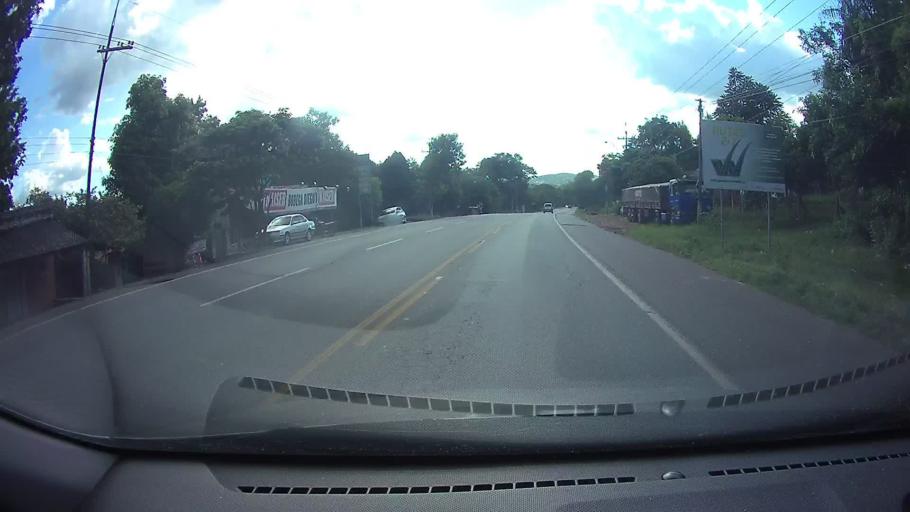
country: PY
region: Cordillera
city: Caacupe
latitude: -25.3880
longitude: -57.1126
